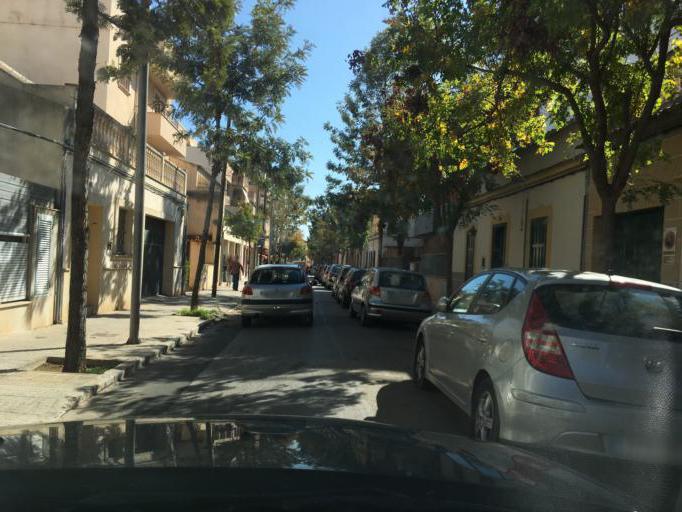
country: ES
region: Balearic Islands
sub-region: Illes Balears
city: Palma
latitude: 39.5854
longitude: 2.6746
